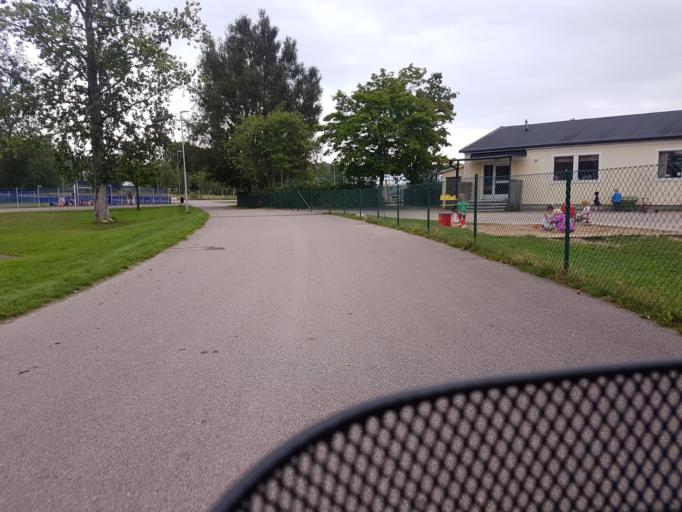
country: SE
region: Vaestra Goetaland
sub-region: Ale Kommun
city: Nodinge-Nol
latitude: 57.8935
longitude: 12.0534
